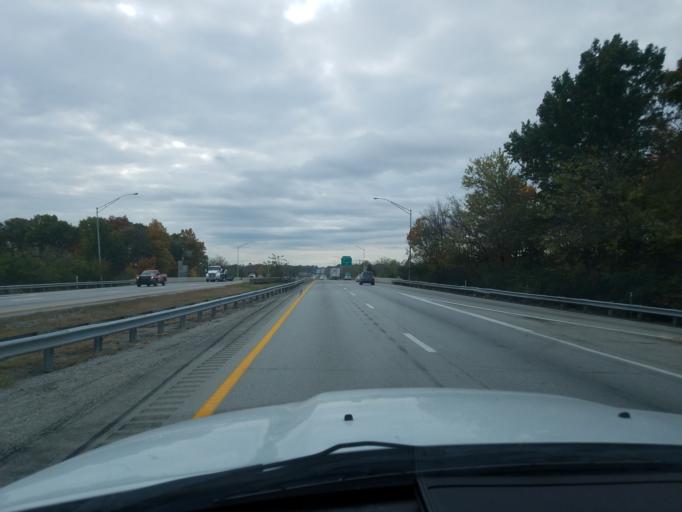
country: US
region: Kentucky
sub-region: Jefferson County
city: Middletown
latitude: 38.2238
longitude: -85.5057
